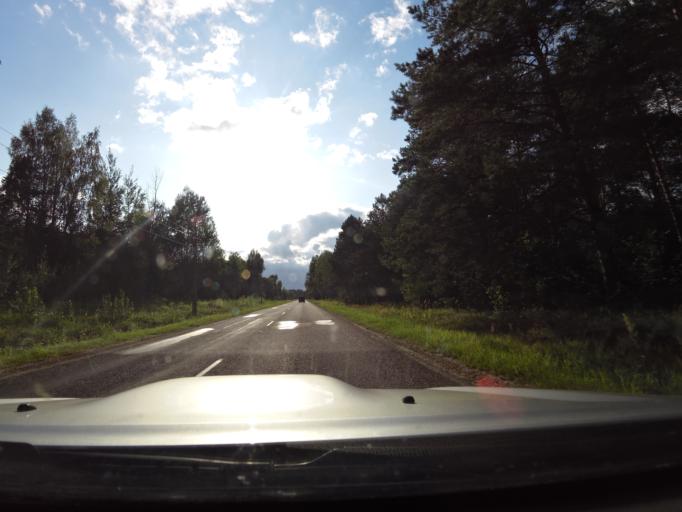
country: LV
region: Nereta
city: Nereta
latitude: 56.1840
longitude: 25.3871
